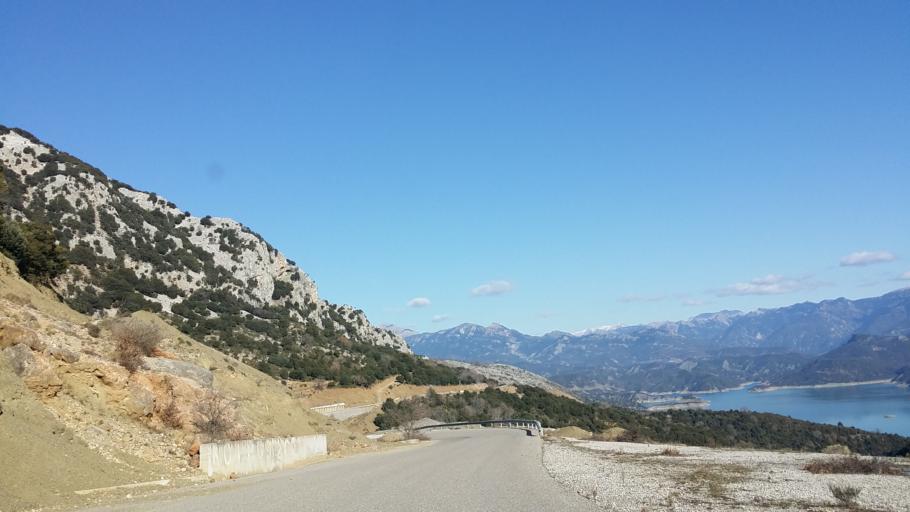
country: GR
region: Central Greece
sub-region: Nomos Evrytanias
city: Kerasochori
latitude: 38.9419
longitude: 21.4581
